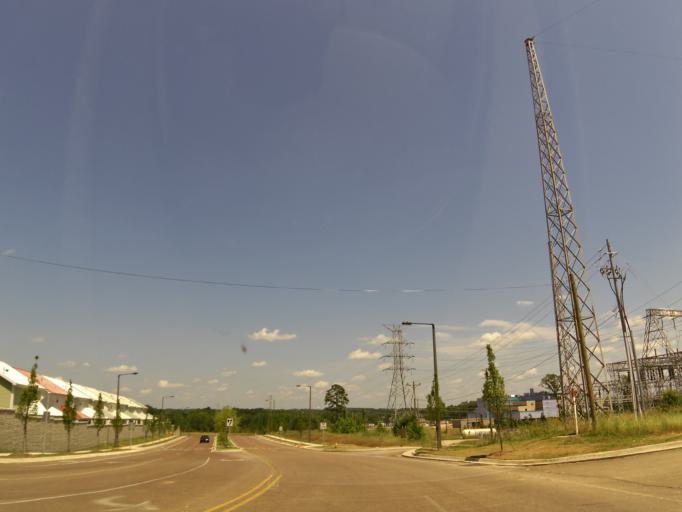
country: US
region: Mississippi
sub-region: Lafayette County
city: University
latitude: 34.3513
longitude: -89.5342
